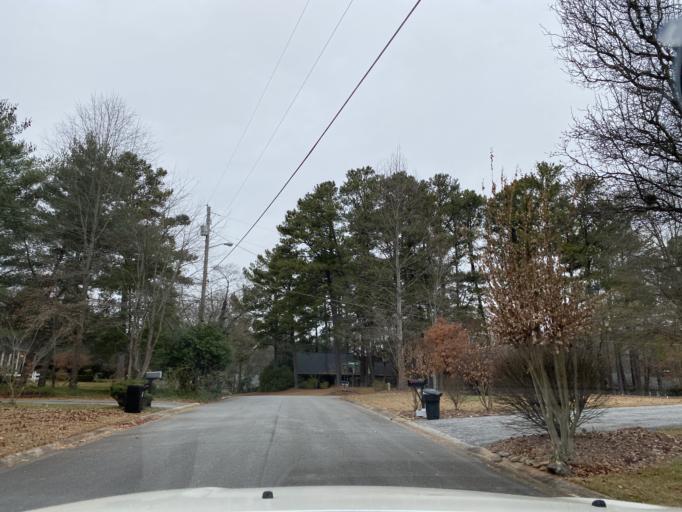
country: US
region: Georgia
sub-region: Cobb County
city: Fair Oaks
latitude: 33.9188
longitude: -84.5684
